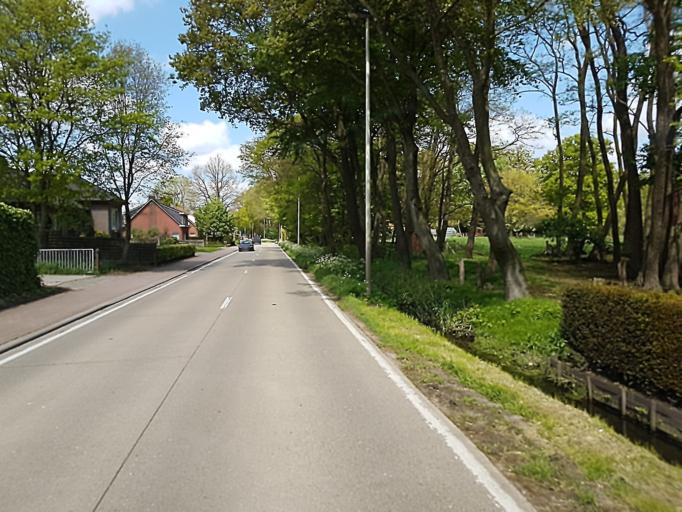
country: BE
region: Flanders
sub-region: Provincie Antwerpen
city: Brecht
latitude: 51.3530
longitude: 4.6953
